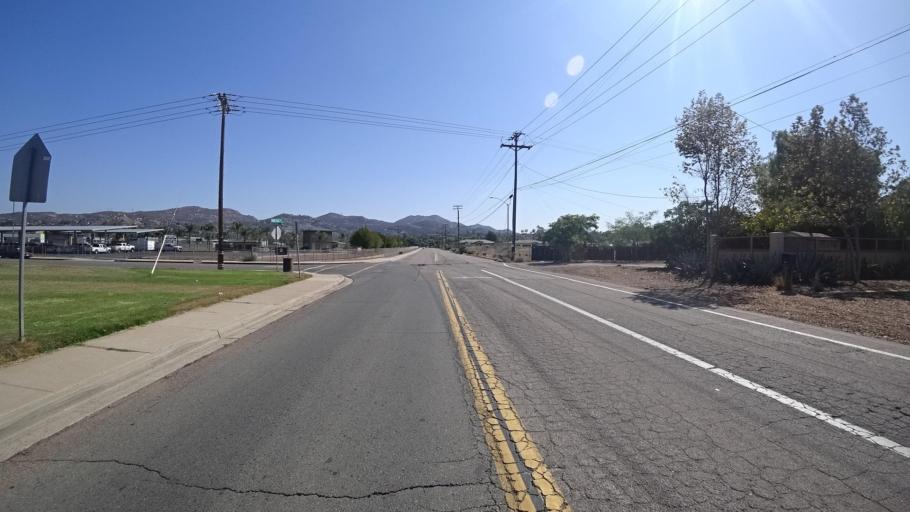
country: US
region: California
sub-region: San Diego County
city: Granite Hills
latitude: 32.7964
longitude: -116.9185
